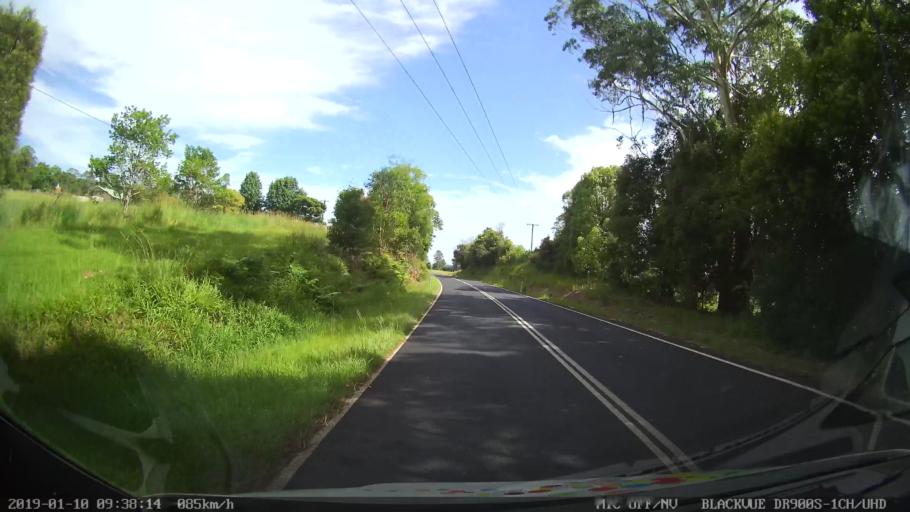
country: AU
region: New South Wales
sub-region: Coffs Harbour
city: Nana Glen
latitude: -30.1786
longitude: 153.0078
